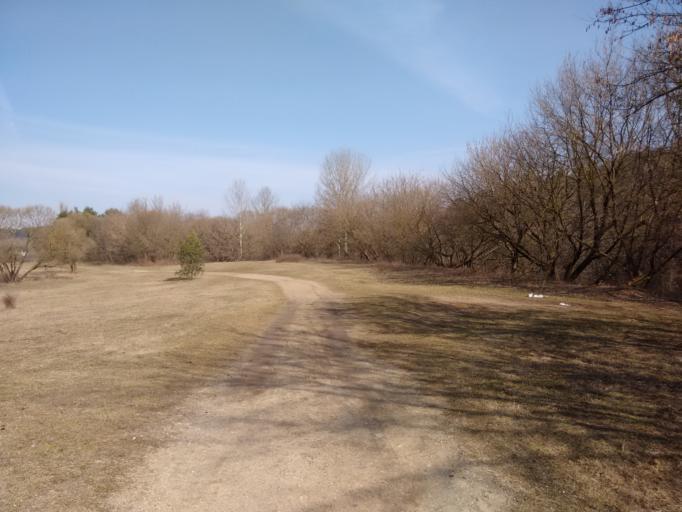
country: LT
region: Vilnius County
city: Vilkpede
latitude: 54.6769
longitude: 25.2306
